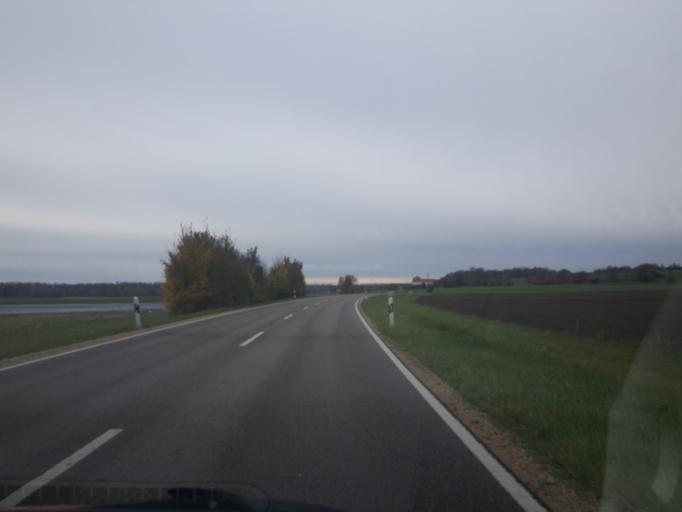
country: DE
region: Bavaria
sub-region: Upper Bavaria
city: Rennertshofen
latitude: 48.7505
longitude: 11.0375
